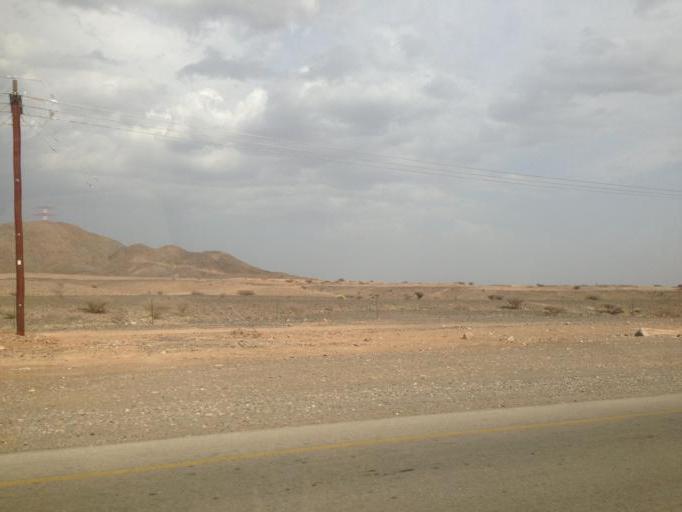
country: OM
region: Ash Sharqiyah
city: Badiyah
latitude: 22.5169
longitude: 58.9483
